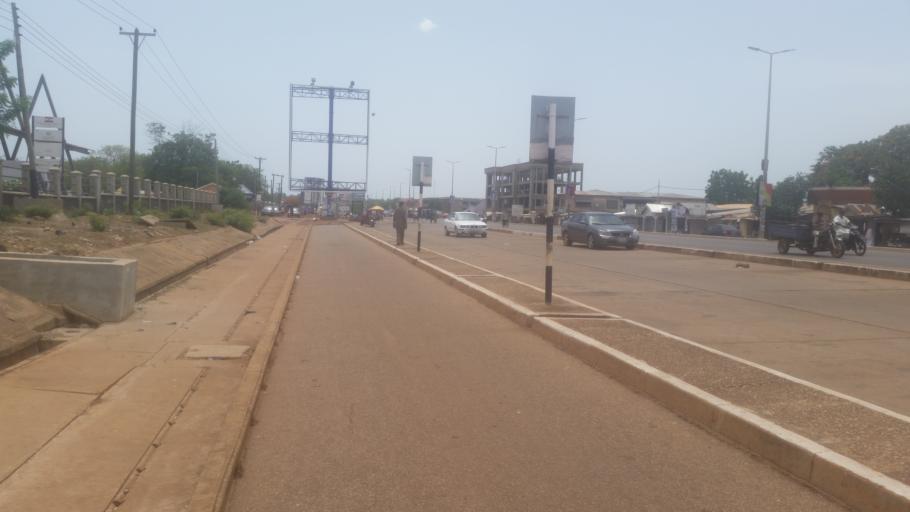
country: GH
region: Northern
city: Tamale
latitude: 9.3936
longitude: -0.8222
